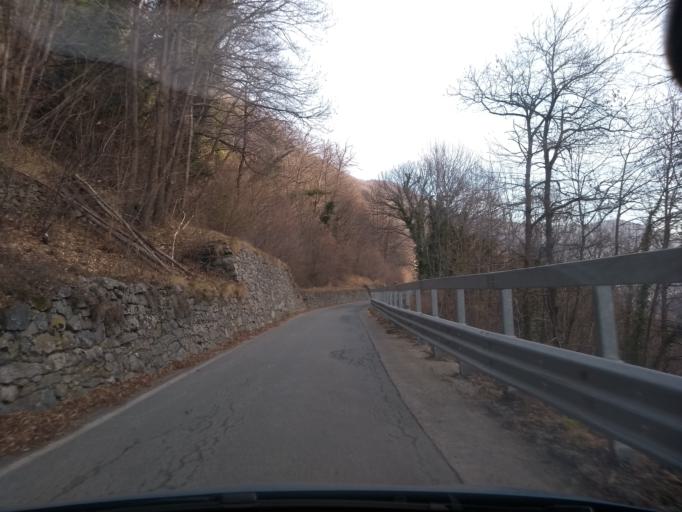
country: IT
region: Piedmont
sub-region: Provincia di Torino
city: Chialamberto
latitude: 45.3218
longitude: 7.3471
